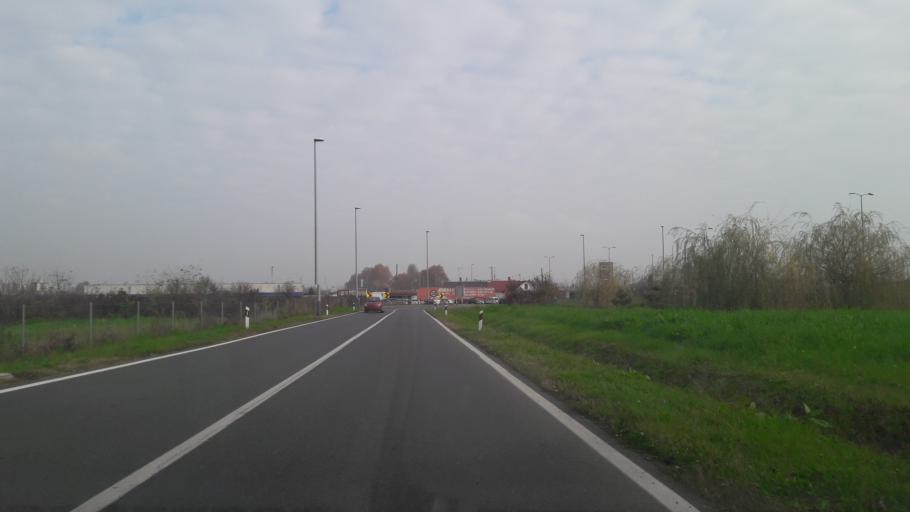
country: HR
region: Osjecko-Baranjska
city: Brijest
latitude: 45.5483
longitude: 18.6619
